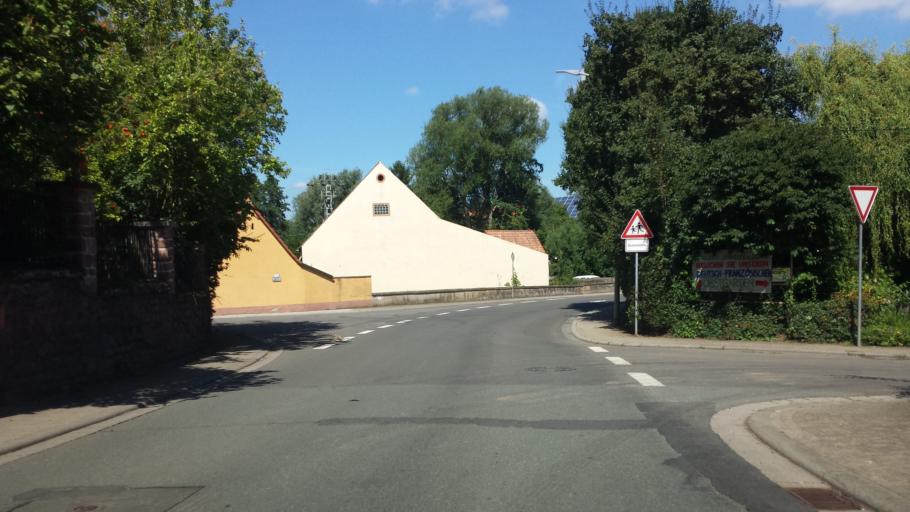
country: DE
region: Rheinland-Pfalz
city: Weitersweiler
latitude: 49.6134
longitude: 7.9982
